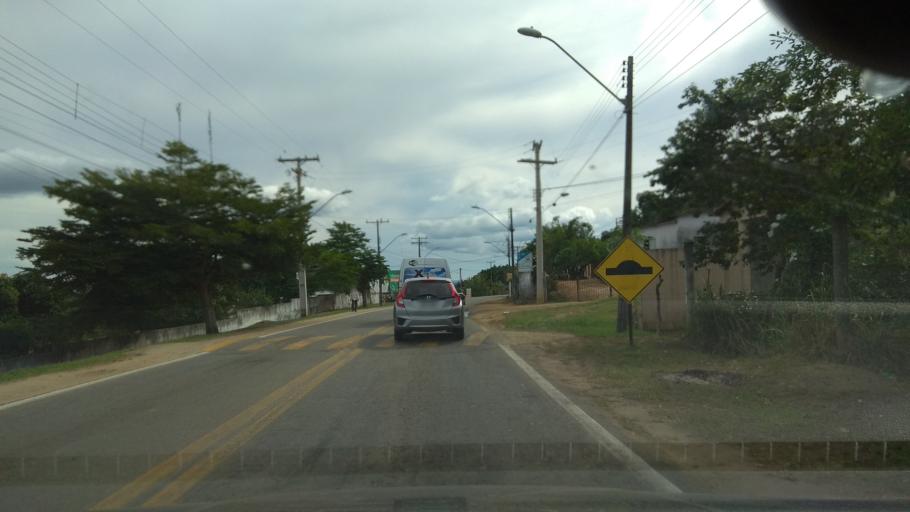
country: BR
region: Bahia
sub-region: Ubata
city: Ubata
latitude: -14.2081
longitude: -39.5985
